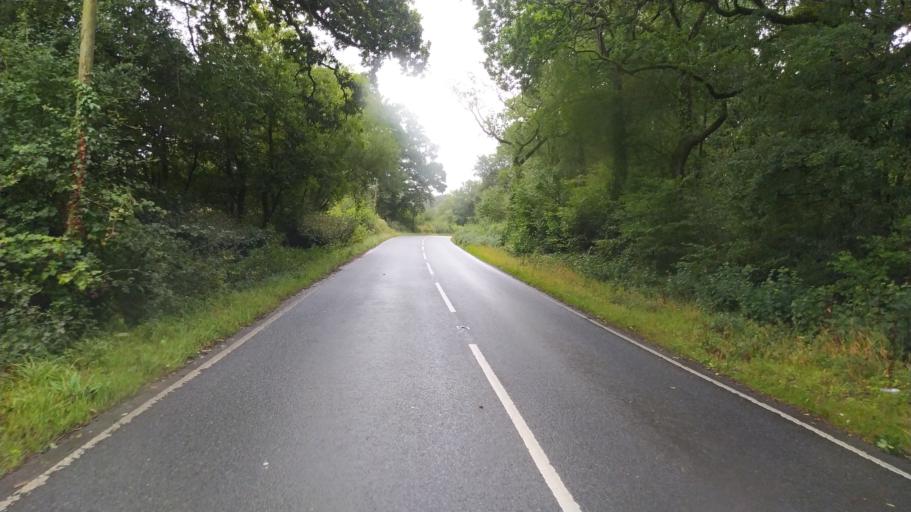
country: GB
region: England
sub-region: Dorset
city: Verwood
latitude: 50.8972
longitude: -1.9358
